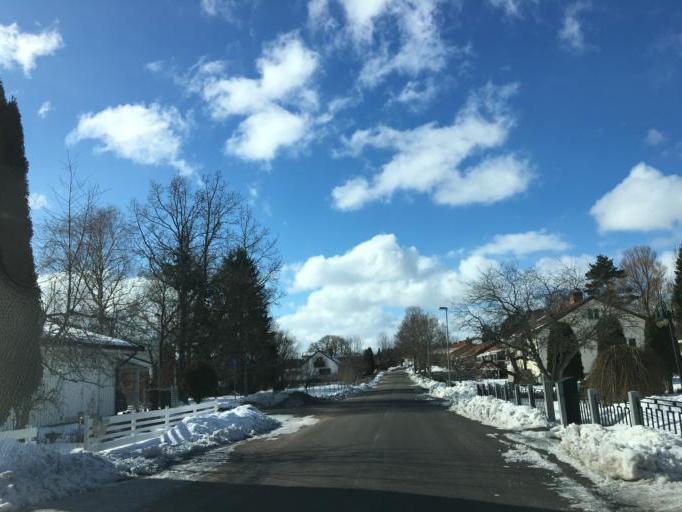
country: SE
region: Soedermanland
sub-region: Eskilstuna Kommun
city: Kvicksund
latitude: 59.5744
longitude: 16.3942
